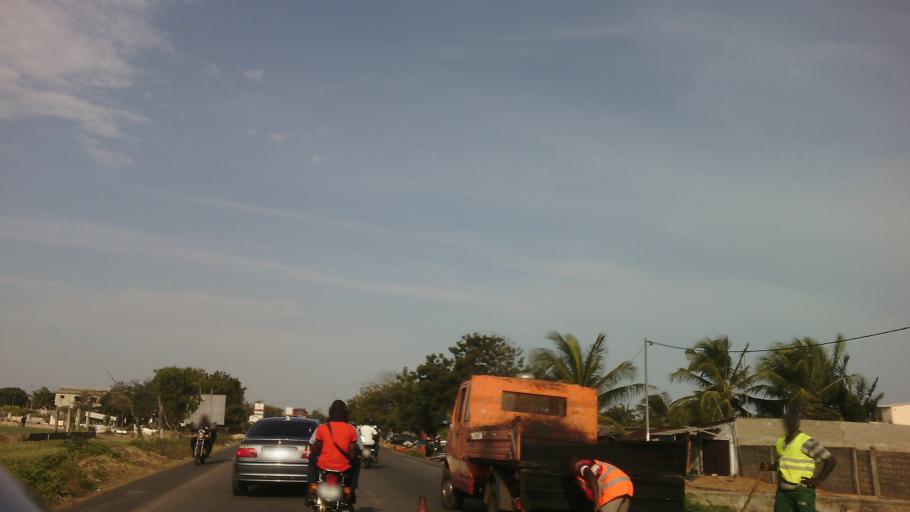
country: TG
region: Maritime
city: Lome
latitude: 6.1769
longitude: 1.3696
